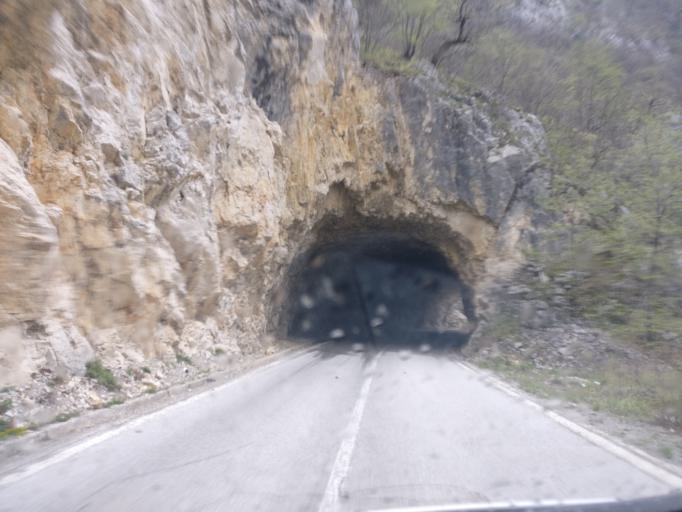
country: ME
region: Opstina Pluzine
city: Pluzine
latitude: 43.2245
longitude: 18.8466
